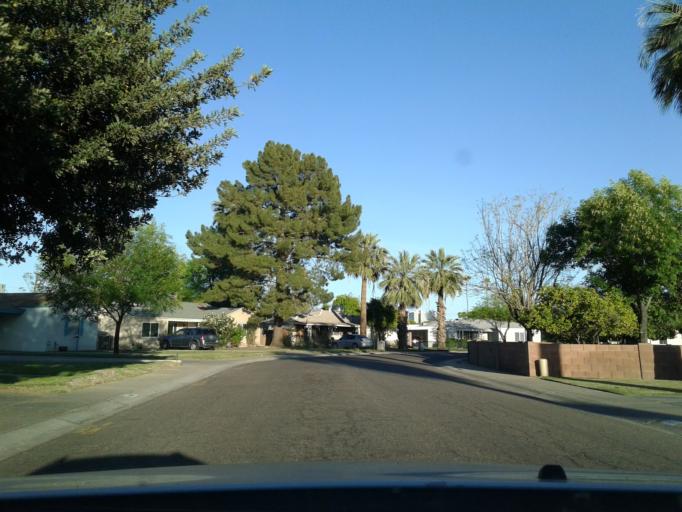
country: US
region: Arizona
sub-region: Maricopa County
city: Phoenix
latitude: 33.5001
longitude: -112.0931
